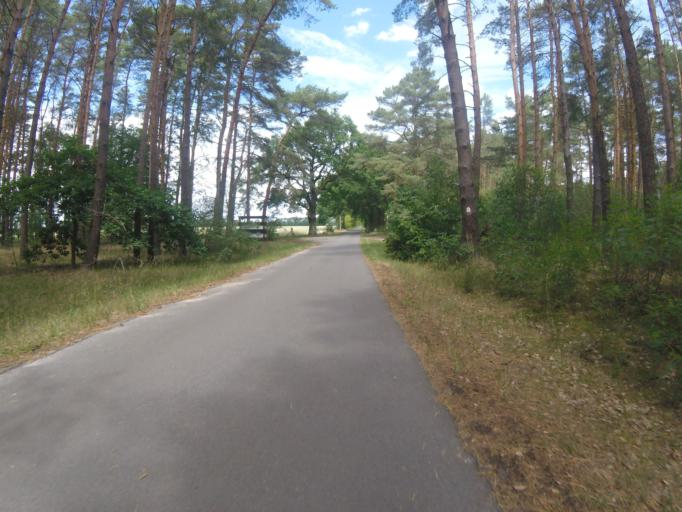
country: DE
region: Brandenburg
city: Bestensee
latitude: 52.2251
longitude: 13.7067
